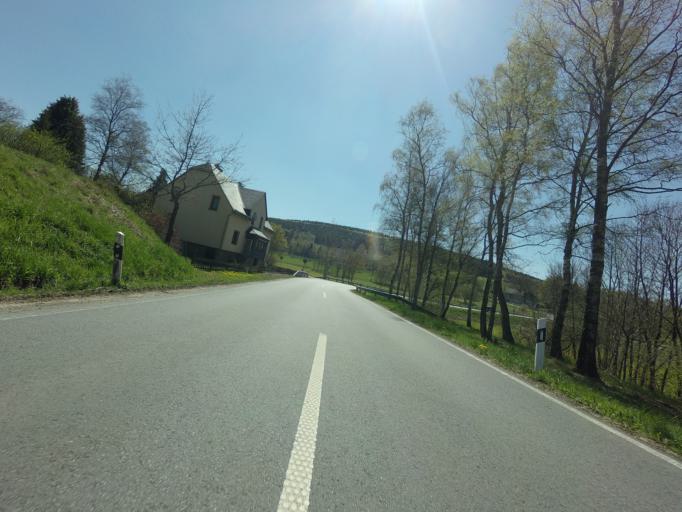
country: DE
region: North Rhine-Westphalia
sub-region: Regierungsbezirk Arnsberg
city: Erndtebruck
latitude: 51.0001
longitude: 8.2661
